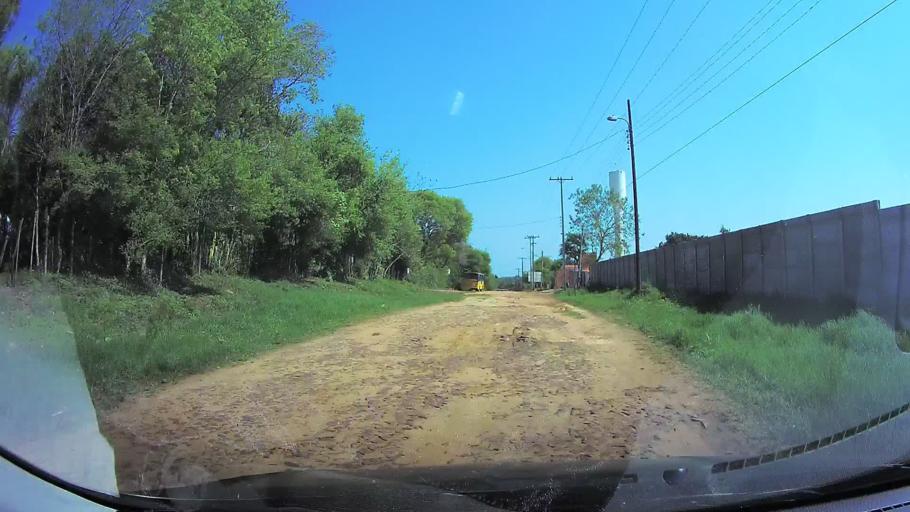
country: PY
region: Central
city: Limpio
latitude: -25.2180
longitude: -57.4842
